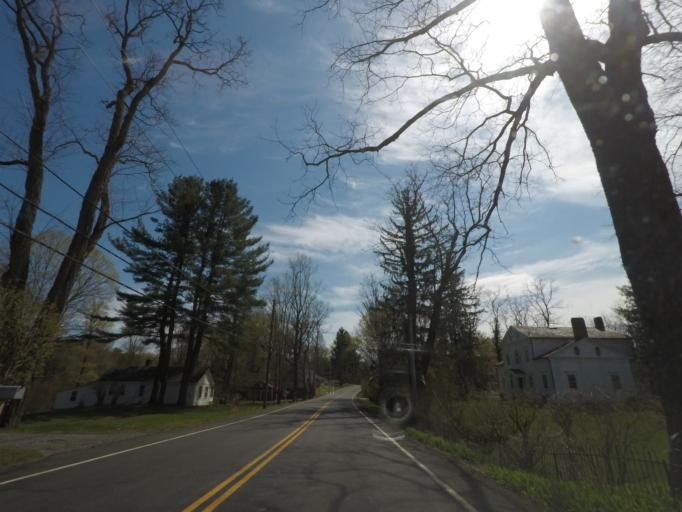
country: US
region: New York
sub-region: Columbia County
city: Chatham
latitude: 42.3948
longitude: -73.5267
